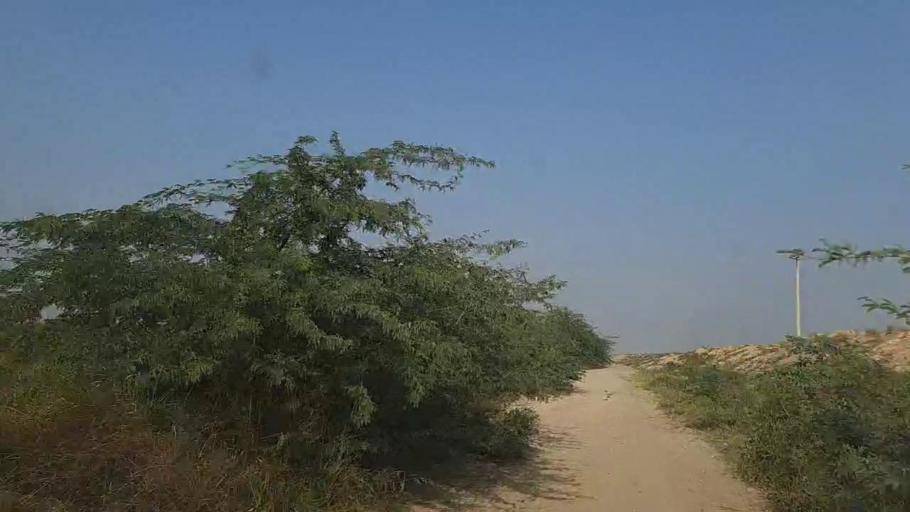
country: PK
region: Sindh
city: Thatta
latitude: 24.6619
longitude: 67.9258
